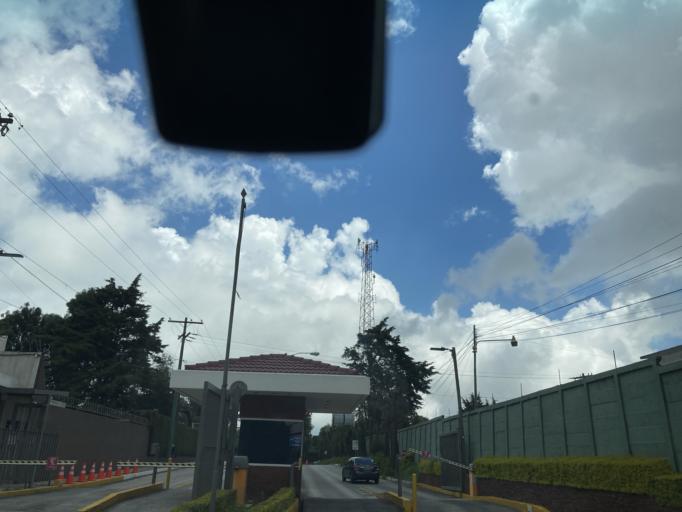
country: GT
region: Guatemala
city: San Jose Pinula
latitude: 14.5439
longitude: -90.4283
